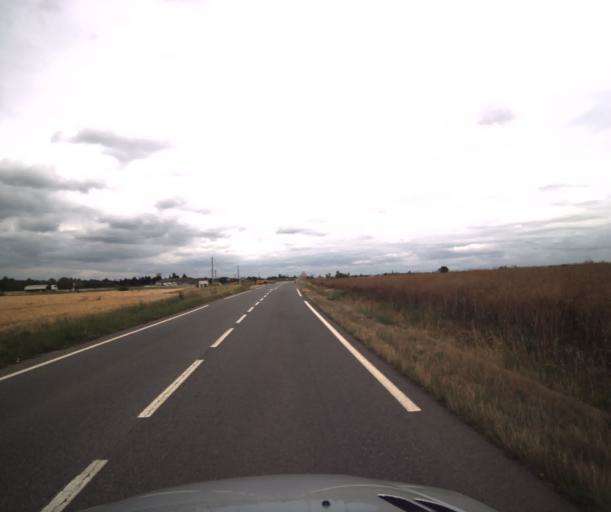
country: FR
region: Midi-Pyrenees
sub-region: Departement de la Haute-Garonne
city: Vernet
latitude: 43.4437
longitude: 1.4145
